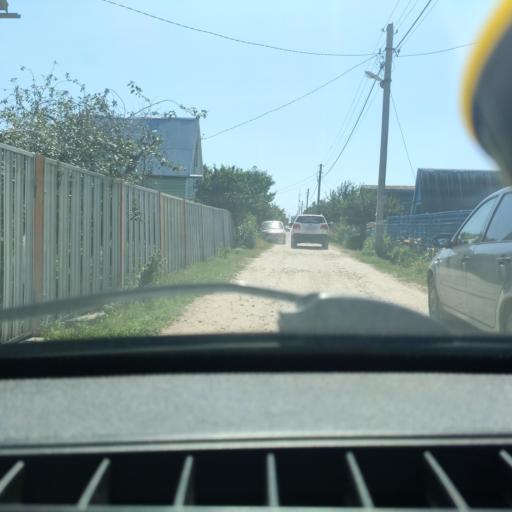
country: RU
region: Samara
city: Tol'yatti
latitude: 53.5944
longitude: 49.3054
